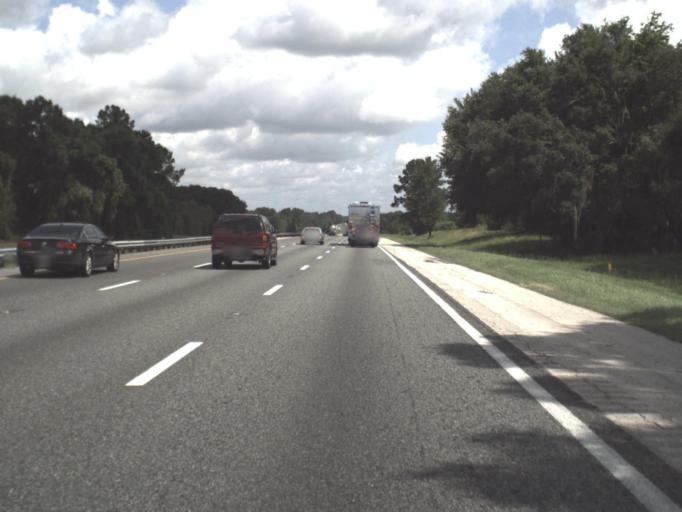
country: US
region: Florida
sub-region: Alachua County
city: High Springs
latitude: 29.9019
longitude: -82.5477
